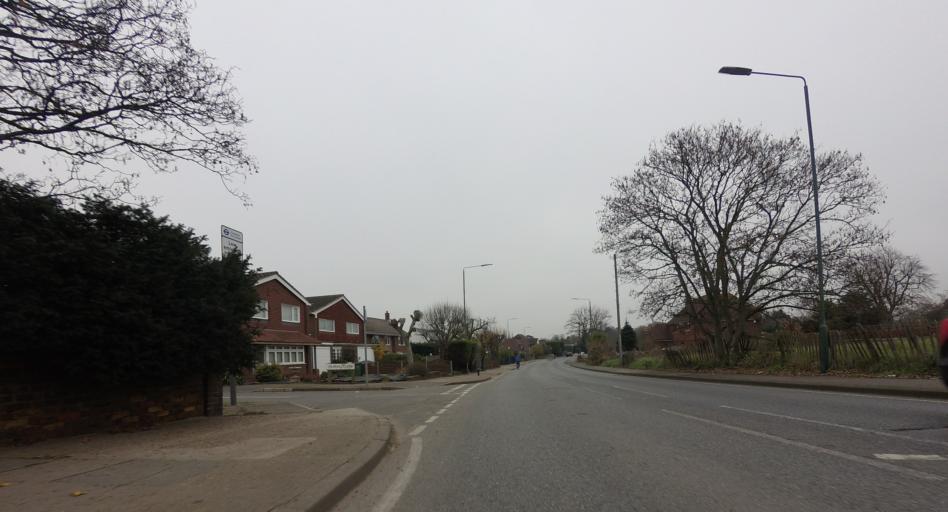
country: GB
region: England
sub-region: Greater London
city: Bexley
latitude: 51.4369
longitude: 0.1633
